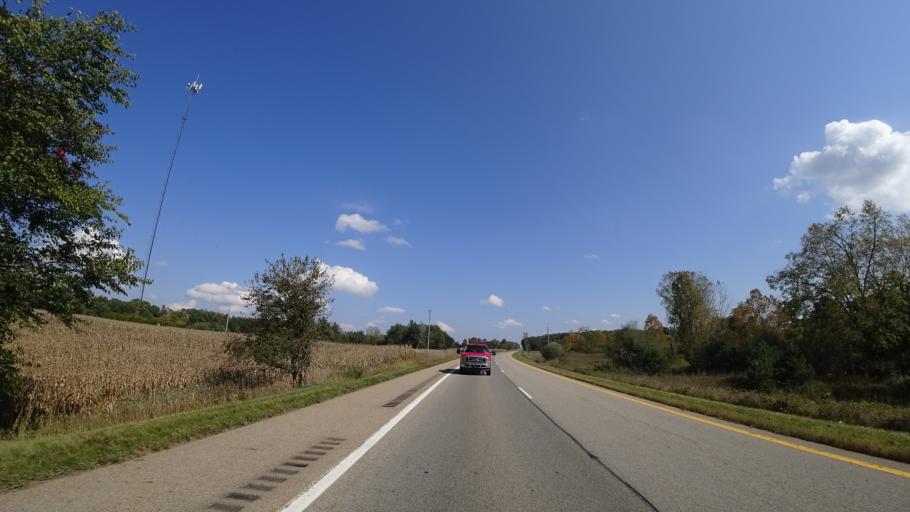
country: US
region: Michigan
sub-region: Calhoun County
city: Homer
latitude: 42.1604
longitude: -84.7663
